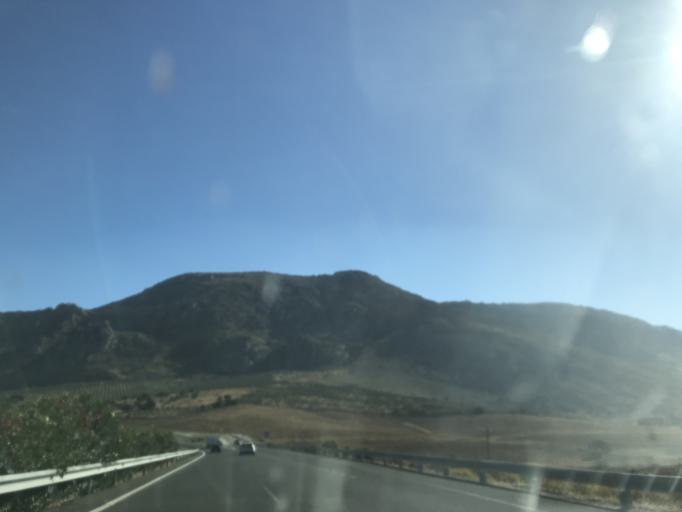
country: ES
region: Andalusia
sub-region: Provincia de Malaga
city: Antequera
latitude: 36.9938
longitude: -4.4716
